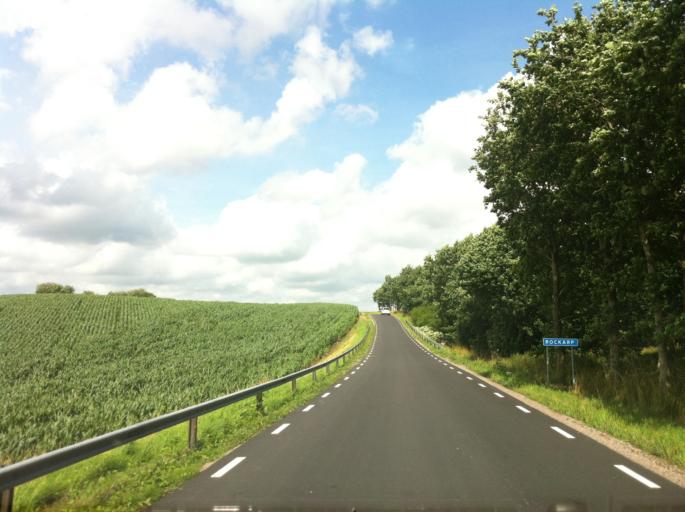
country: SE
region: Skane
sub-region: Trelleborgs Kommun
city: Anderslov
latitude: 55.4480
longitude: 13.3623
